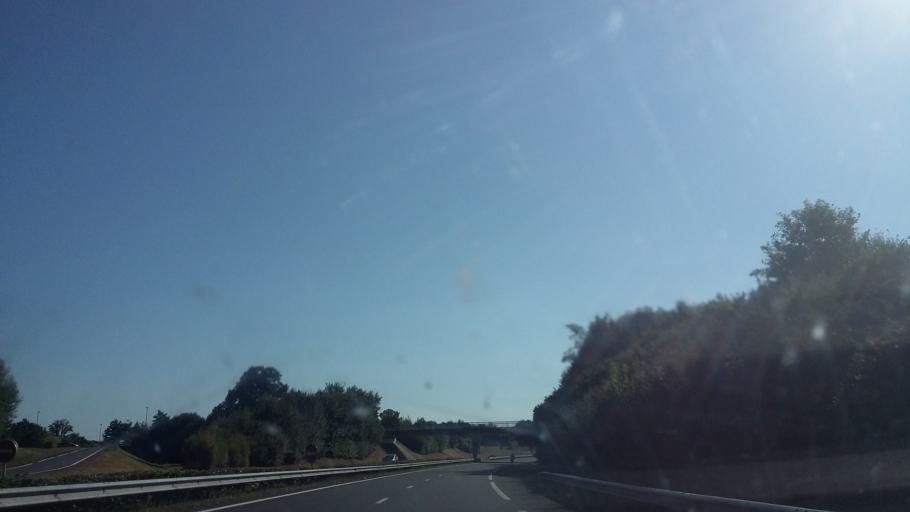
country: FR
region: Pays de la Loire
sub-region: Departement de la Vendee
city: Challans
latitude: 46.8595
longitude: -1.8794
